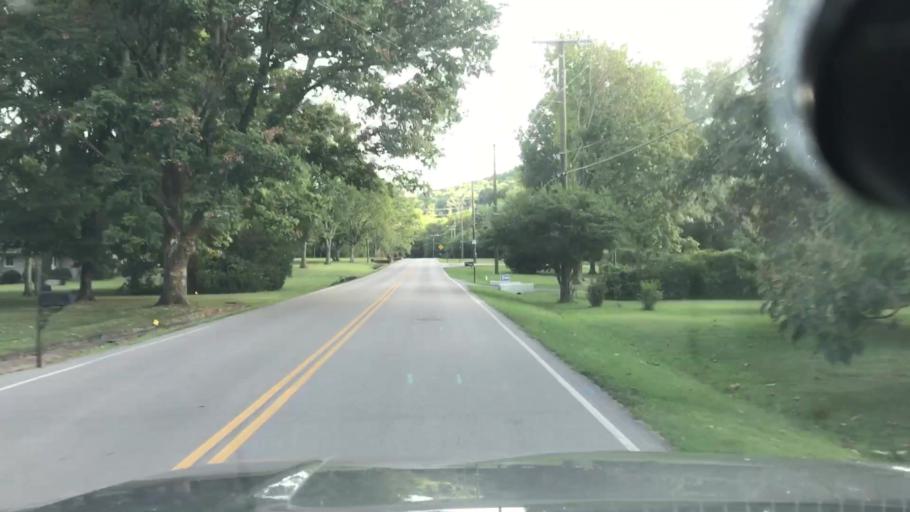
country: US
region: Tennessee
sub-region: Davidson County
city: Forest Hills
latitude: 36.0613
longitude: -86.8460
